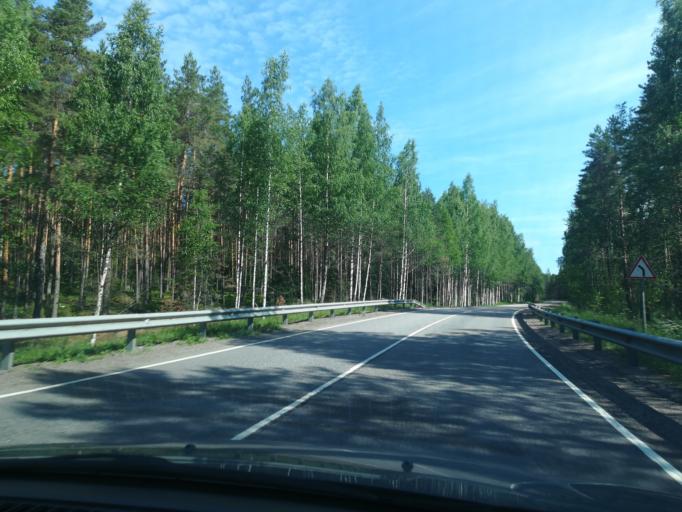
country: RU
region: Leningrad
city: Lesogorskiy
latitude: 60.9243
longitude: 28.8881
